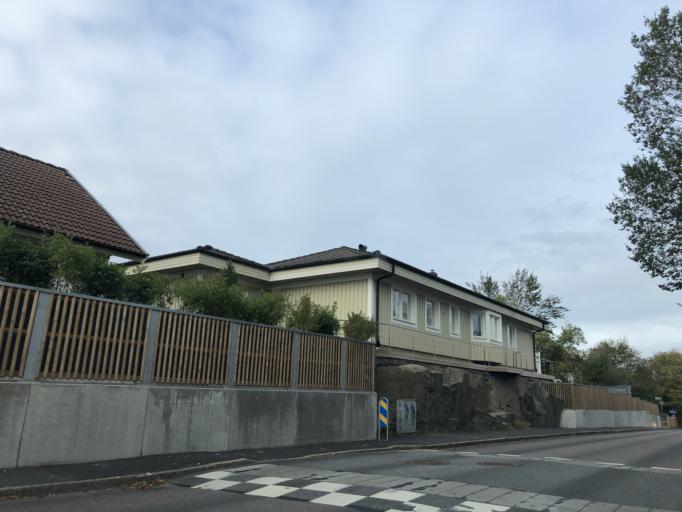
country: SE
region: Vaestra Goetaland
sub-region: Goteborg
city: Majorna
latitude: 57.6797
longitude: 11.8888
